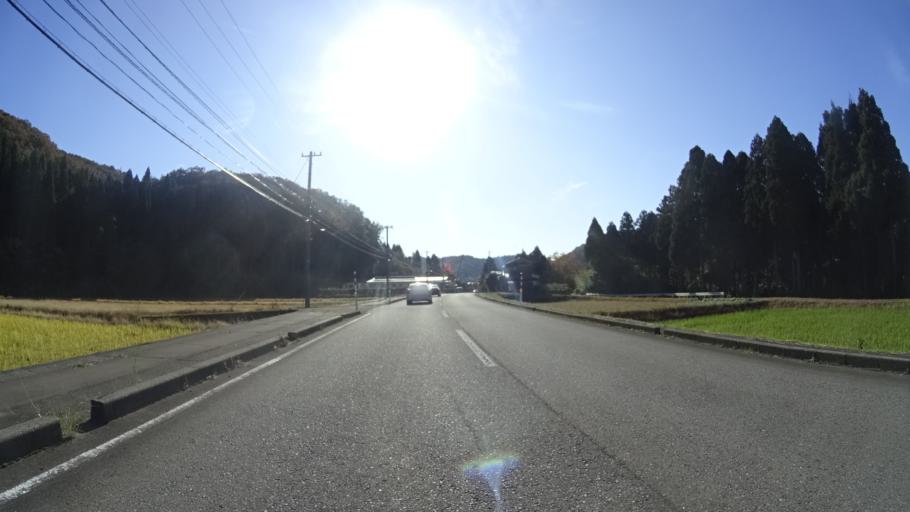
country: JP
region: Ishikawa
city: Komatsu
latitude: 36.3885
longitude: 136.5276
